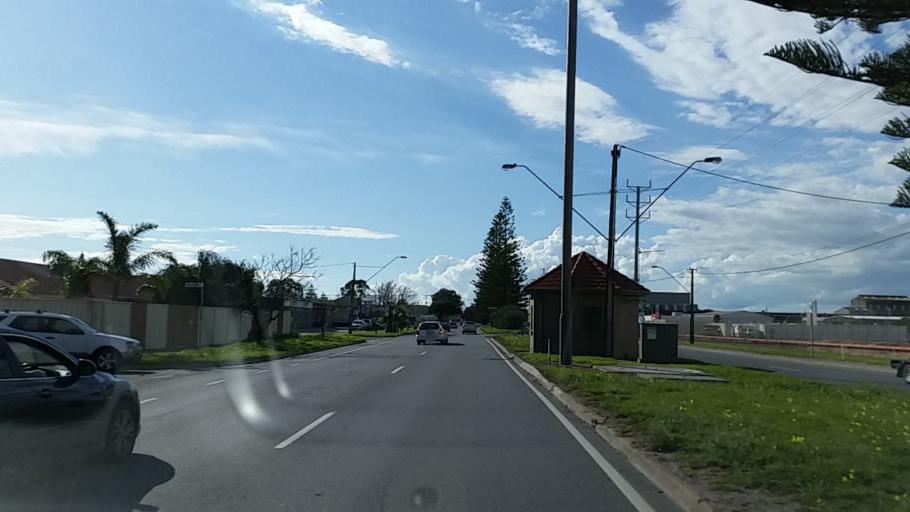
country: AU
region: South Australia
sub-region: Port Adelaide Enfield
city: Birkenhead
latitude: -34.8274
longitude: 138.5005
